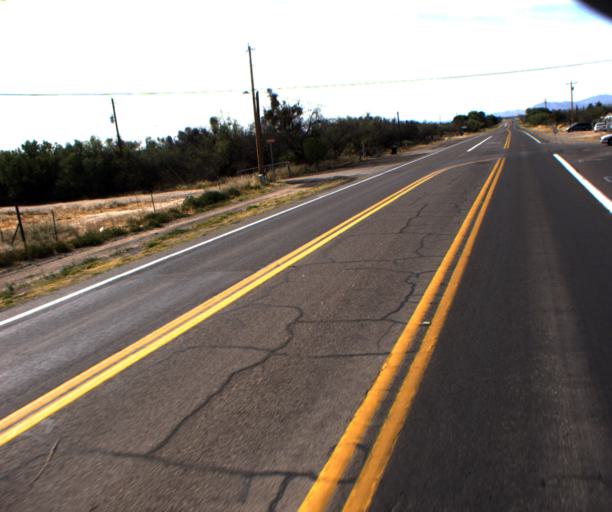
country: US
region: Arizona
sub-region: Graham County
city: Cactus Flat
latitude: 32.7666
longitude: -109.7164
